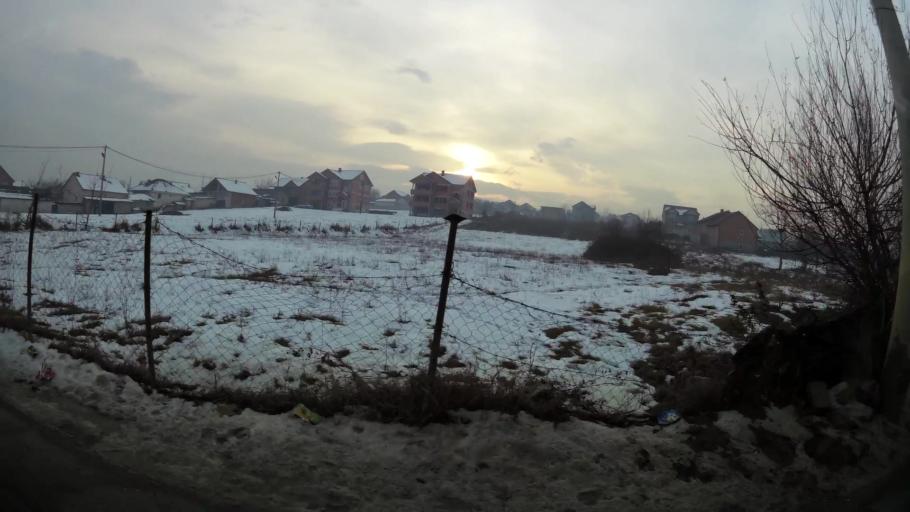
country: MK
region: Suto Orizari
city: Suto Orizare
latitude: 42.0372
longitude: 21.4200
